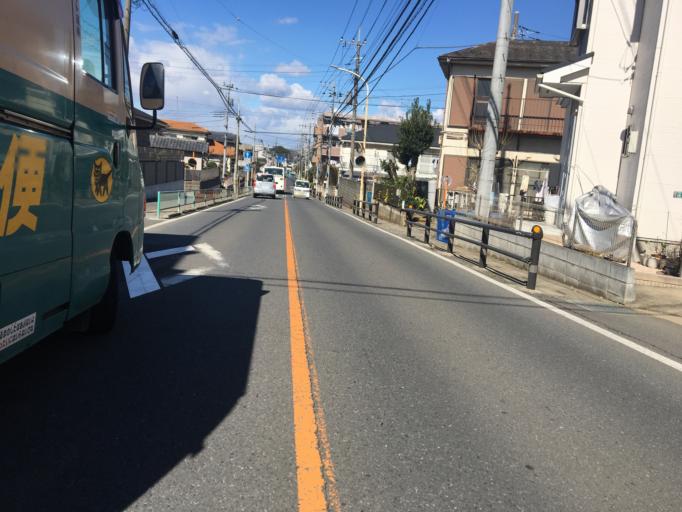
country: JP
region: Saitama
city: Shiki
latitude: 35.8088
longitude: 139.5534
